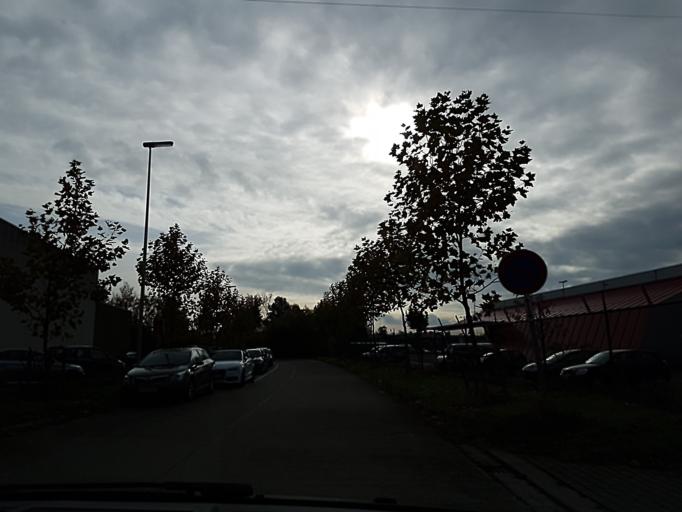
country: BE
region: Flanders
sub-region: Provincie Antwerpen
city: Lier
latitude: 51.1468
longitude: 4.5557
